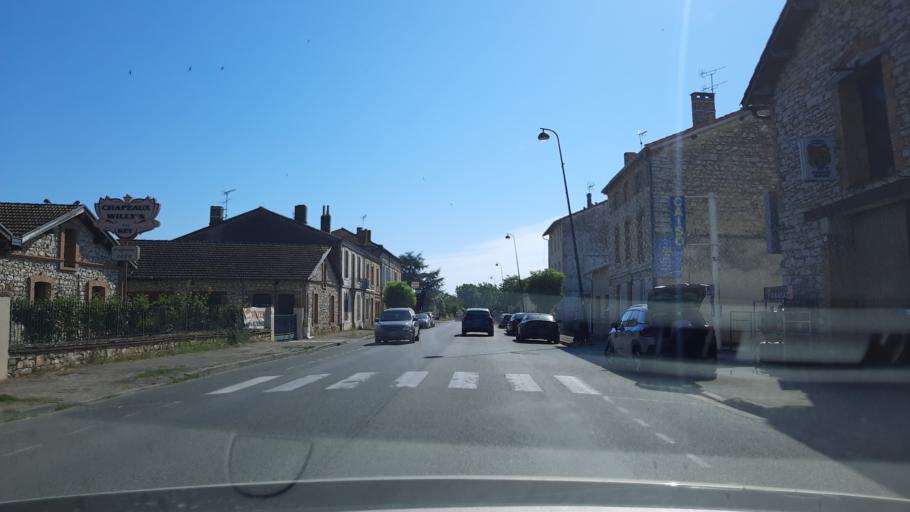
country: FR
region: Midi-Pyrenees
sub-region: Departement du Tarn-et-Garonne
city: Caussade
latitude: 44.1619
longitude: 1.5438
